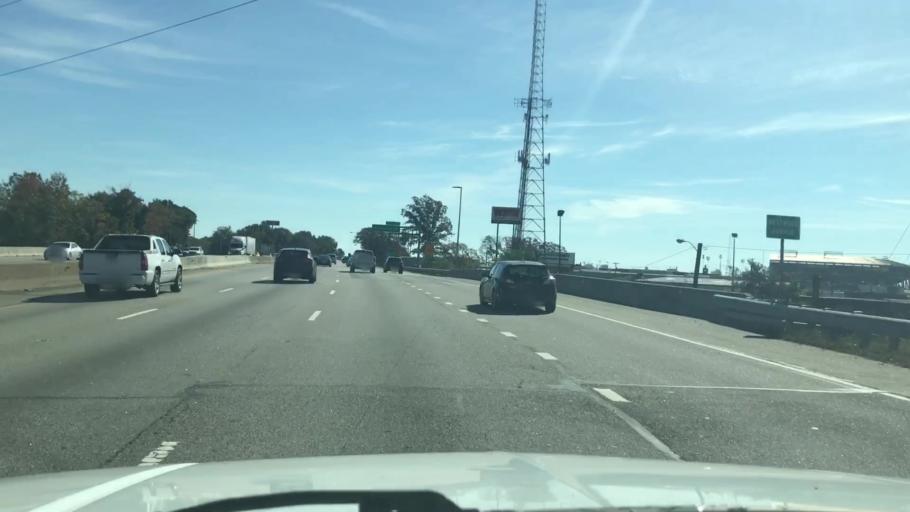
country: US
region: Virginia
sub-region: City of Richmond
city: Richmond
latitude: 37.5785
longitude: -77.4671
